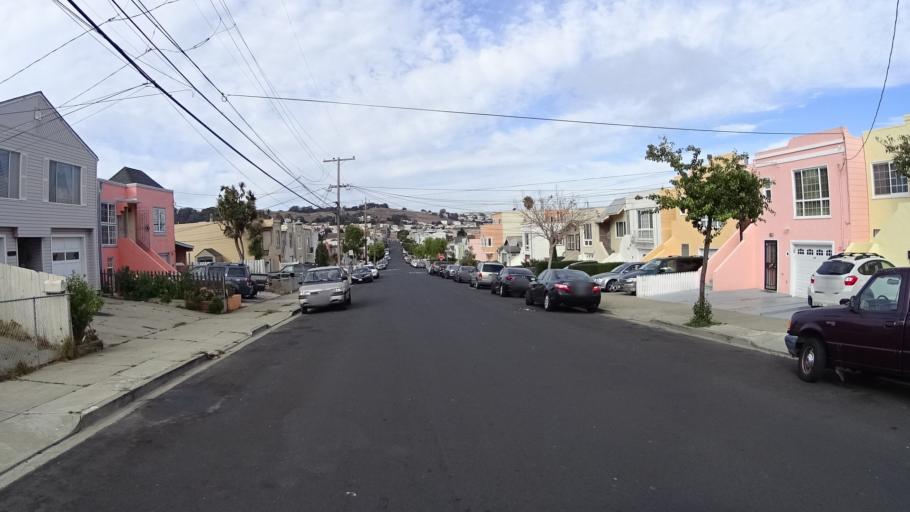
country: US
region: California
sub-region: San Mateo County
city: Brisbane
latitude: 37.7025
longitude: -122.4169
